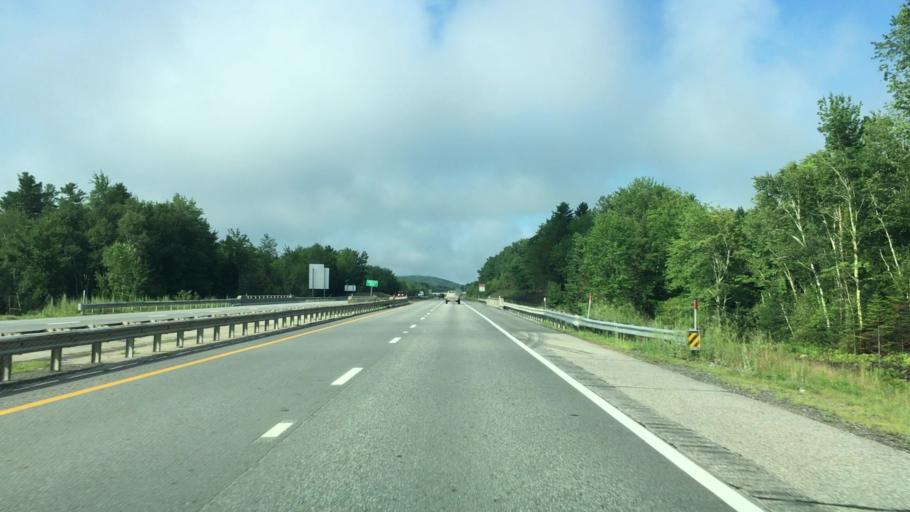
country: US
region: Maine
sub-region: Androscoggin County
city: Sabattus
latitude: 44.0927
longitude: -70.0989
